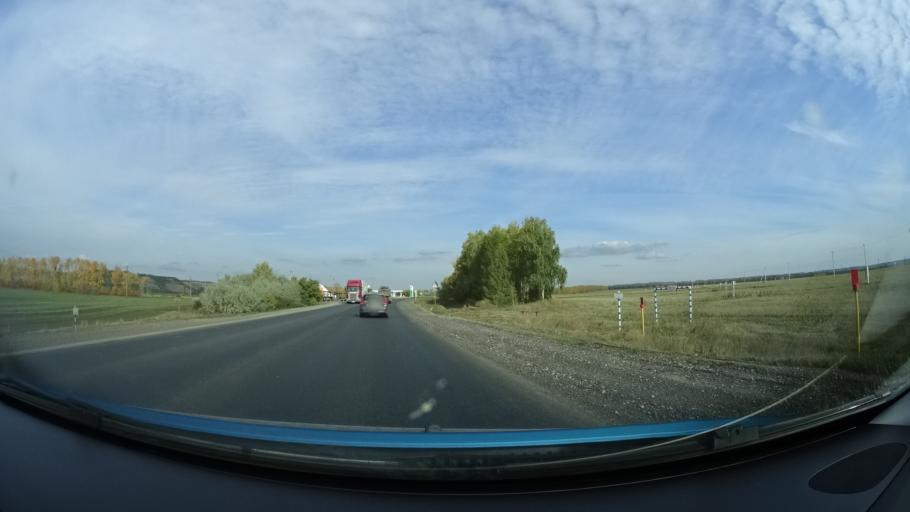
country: RU
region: Bashkortostan
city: Kandry
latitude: 54.5299
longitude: 54.0693
